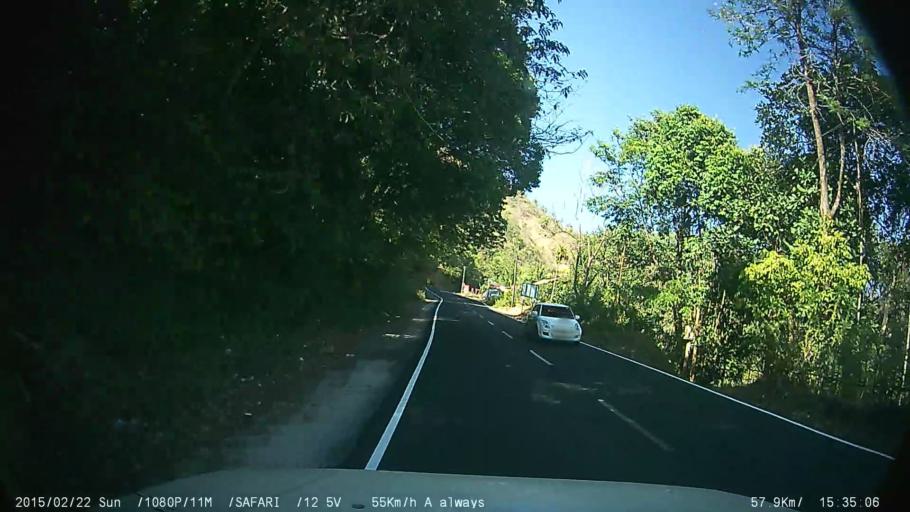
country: IN
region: Kerala
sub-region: Kottayam
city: Erattupetta
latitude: 9.5558
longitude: 76.9744
